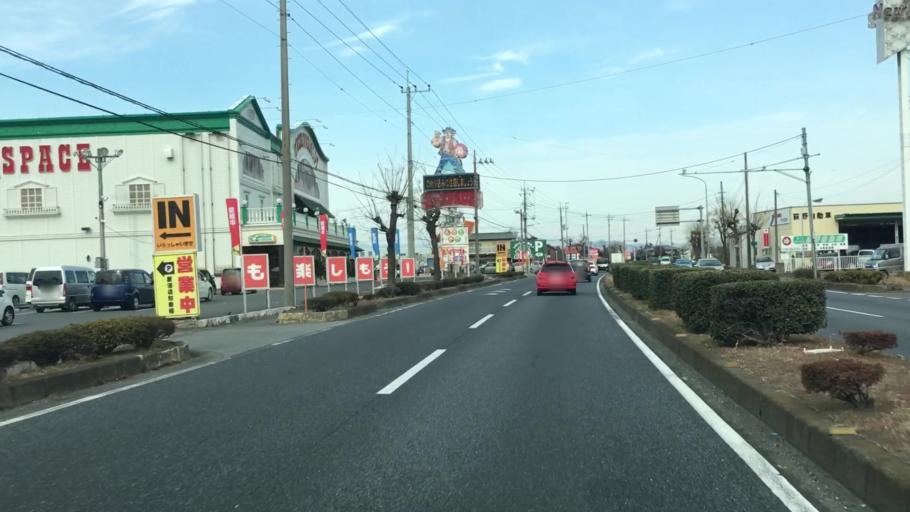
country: JP
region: Saitama
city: Menuma
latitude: 36.2298
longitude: 139.3710
